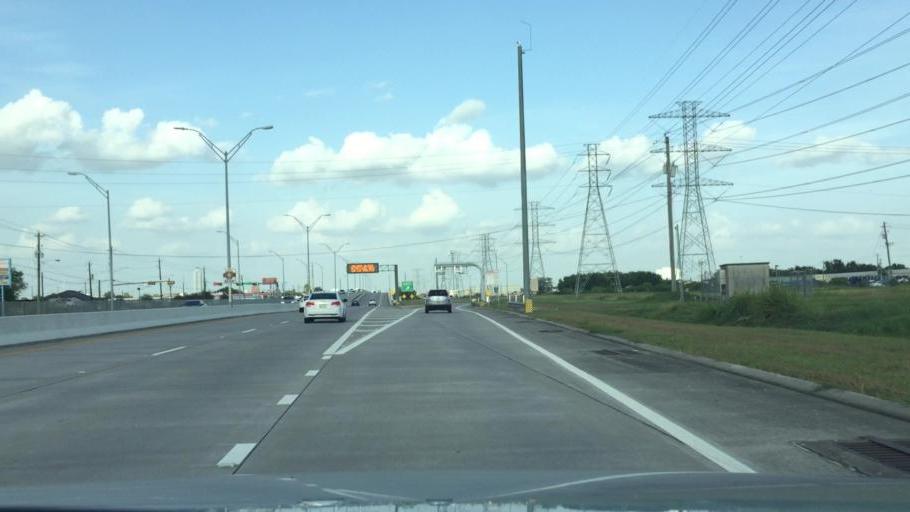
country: US
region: Texas
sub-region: Harris County
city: Piney Point Village
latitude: 29.7191
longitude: -95.5239
